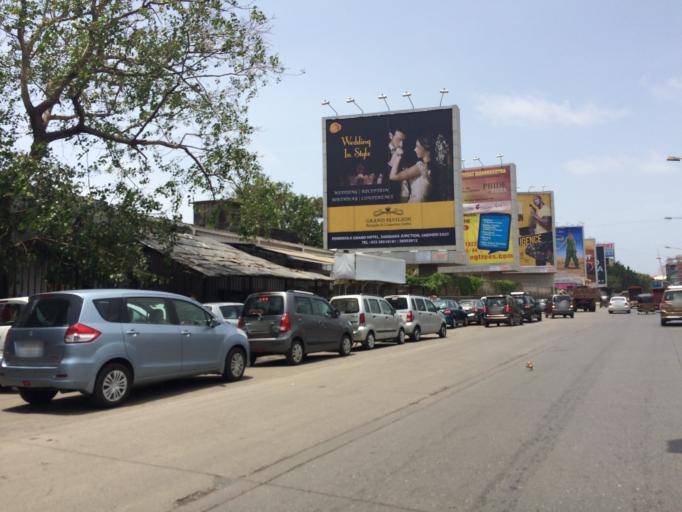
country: IN
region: Maharashtra
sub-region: Mumbai Suburban
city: Powai
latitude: 19.1343
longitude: 72.8319
